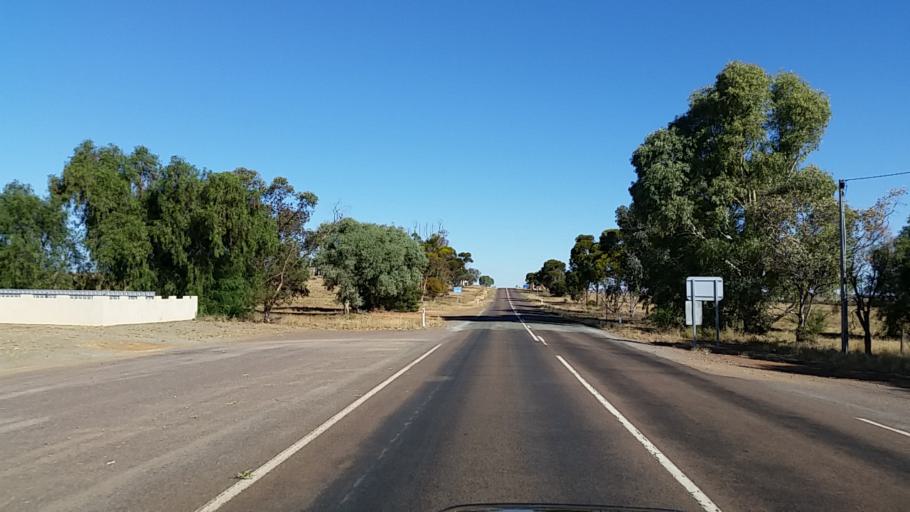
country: AU
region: South Australia
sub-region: Flinders Ranges
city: Quorn
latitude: -32.4248
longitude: 138.5306
